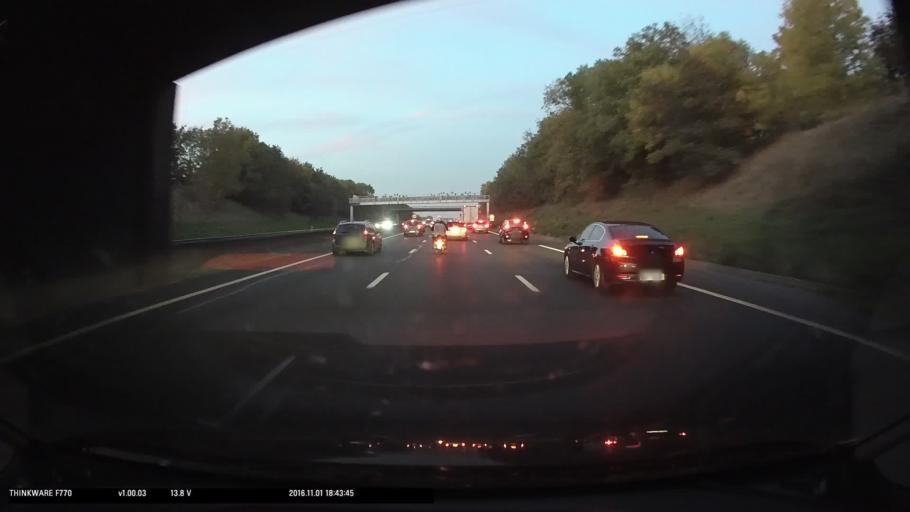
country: FR
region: Ile-de-France
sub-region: Departement de l'Essonne
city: Chilly-Mazarin
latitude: 48.7098
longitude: 2.3072
